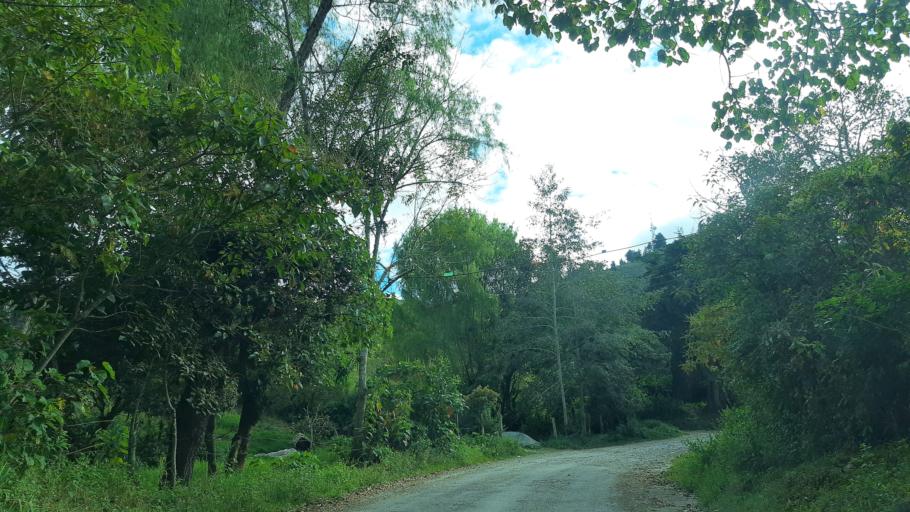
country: CO
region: Cundinamarca
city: Tenza
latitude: 5.0422
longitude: -73.4231
